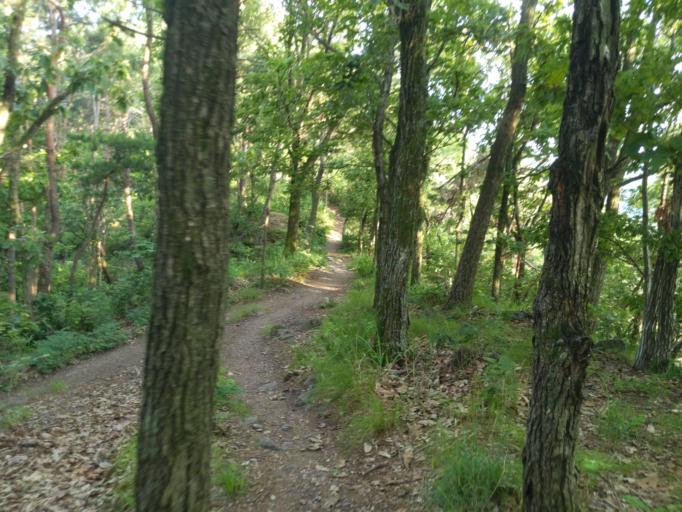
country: KR
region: Daegu
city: Hwawon
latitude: 35.7825
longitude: 128.5473
